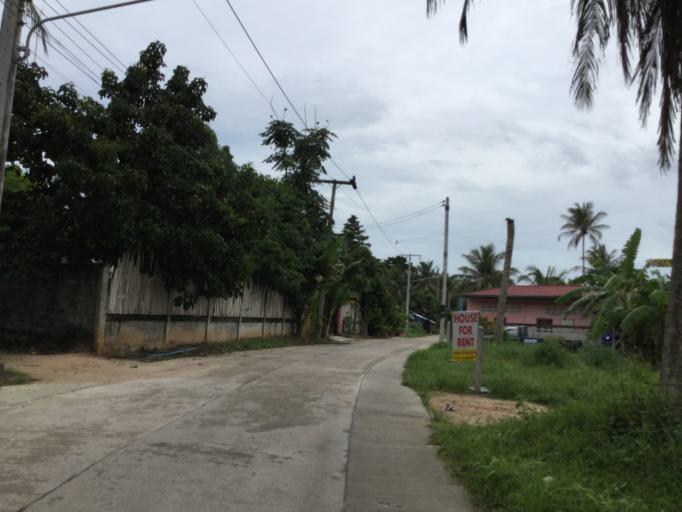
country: TH
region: Surat Thani
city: Ko Pha-Ngan
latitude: 9.7206
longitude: 100.0075
